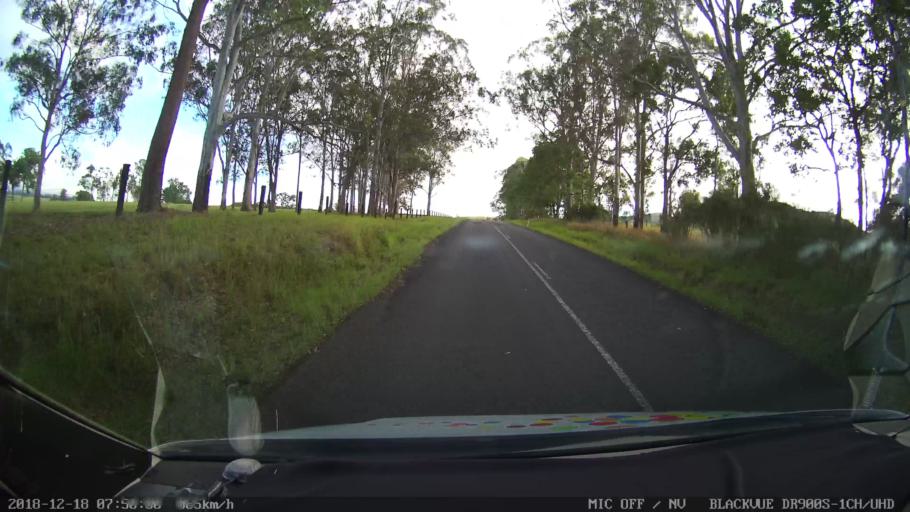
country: AU
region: New South Wales
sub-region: Kyogle
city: Kyogle
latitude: -28.4491
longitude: 152.5726
